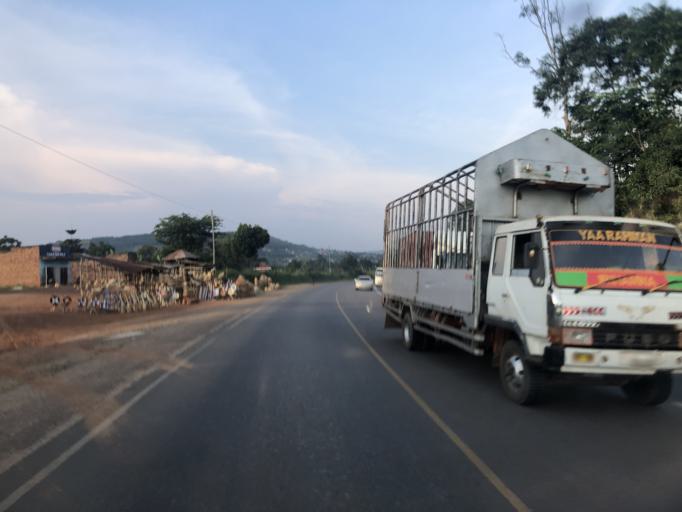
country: UG
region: Central Region
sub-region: Mpigi District
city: Mpigi
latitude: 0.2019
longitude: 32.3014
